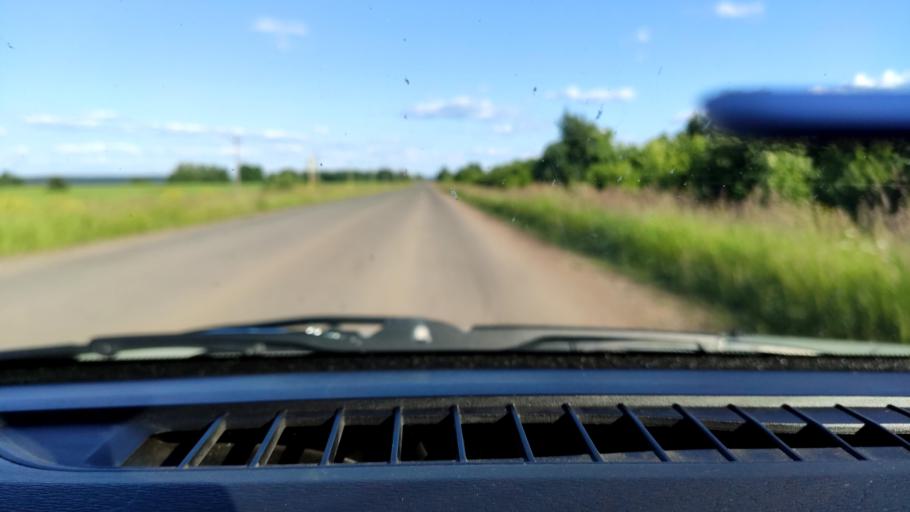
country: RU
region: Perm
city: Uinskoye
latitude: 57.1039
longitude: 56.5364
